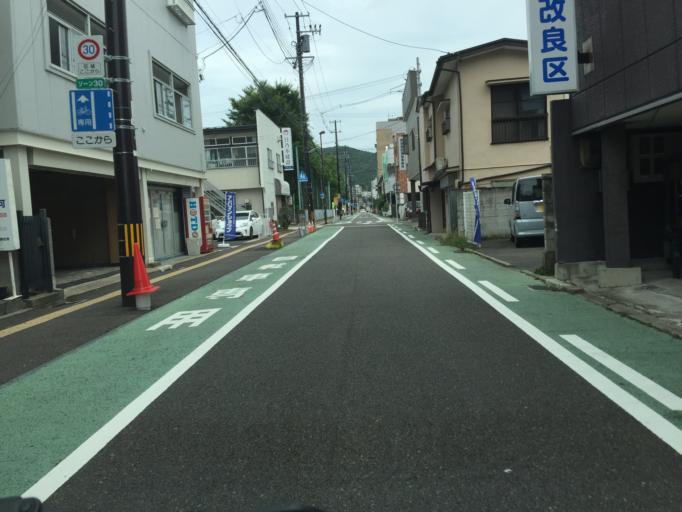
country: JP
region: Fukushima
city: Fukushima-shi
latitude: 37.7579
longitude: 140.4740
